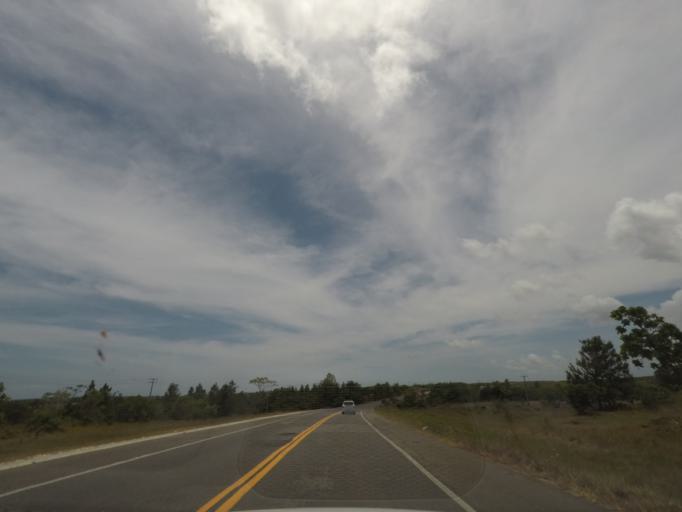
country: BR
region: Bahia
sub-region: Conde
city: Conde
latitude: -11.8643
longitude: -37.6313
